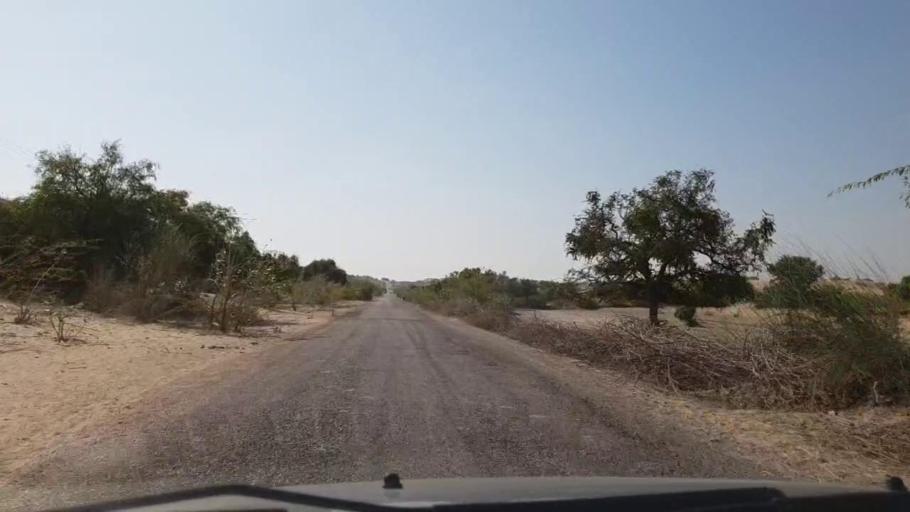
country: PK
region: Sindh
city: Diplo
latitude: 24.5304
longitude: 69.6302
